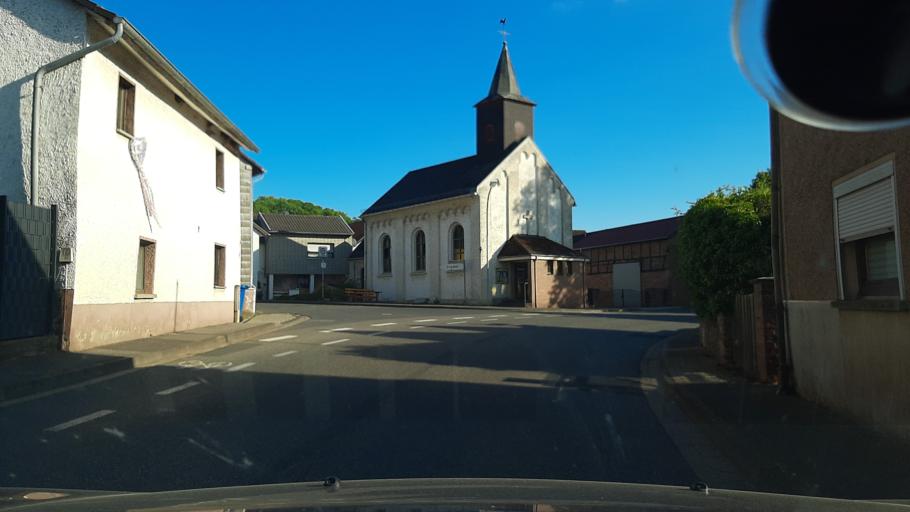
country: DE
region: North Rhine-Westphalia
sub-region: Regierungsbezirk Koln
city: Mechernich
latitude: 50.5798
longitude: 6.6756
